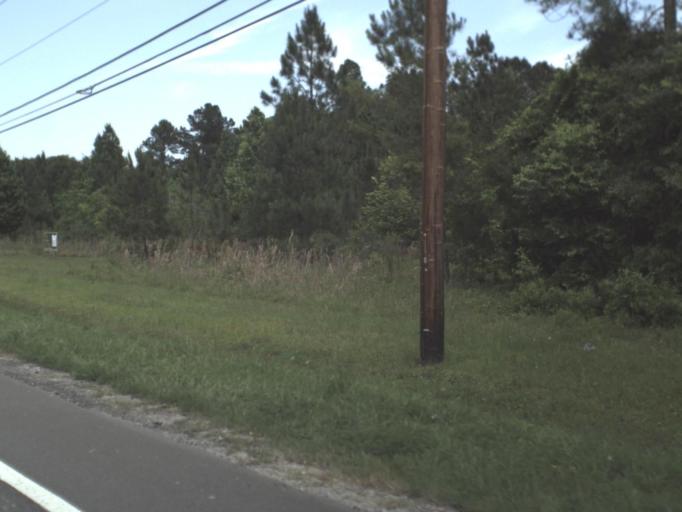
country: US
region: Florida
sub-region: Duval County
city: Jacksonville
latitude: 30.4778
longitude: -81.6292
